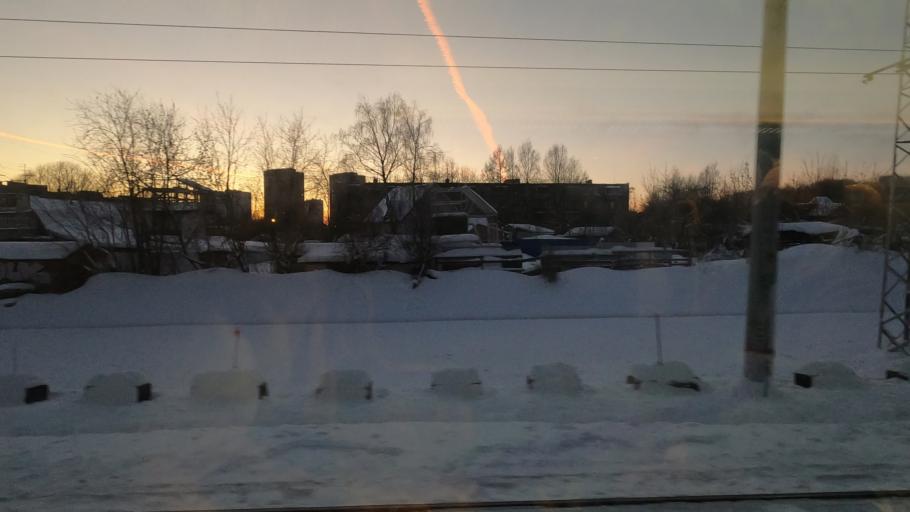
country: RU
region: Moskovskaya
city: Lobnya
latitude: 56.0073
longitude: 37.4877
